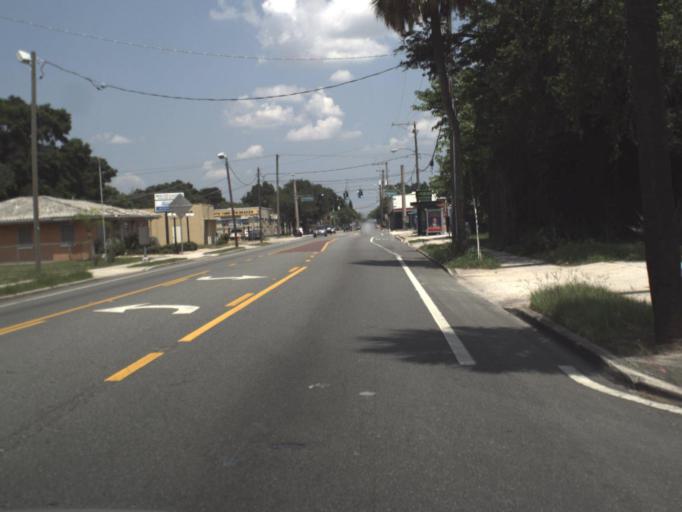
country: US
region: Florida
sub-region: Hillsborough County
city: Tampa
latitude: 27.9654
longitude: -82.4512
